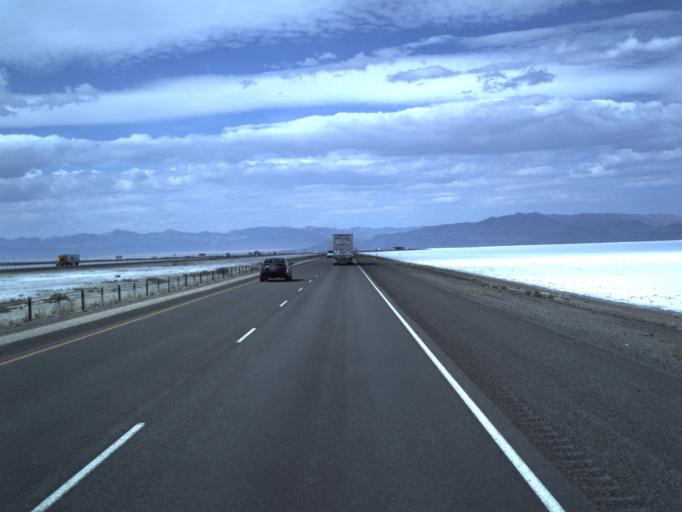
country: US
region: Utah
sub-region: Tooele County
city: Wendover
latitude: 40.7391
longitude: -113.8361
